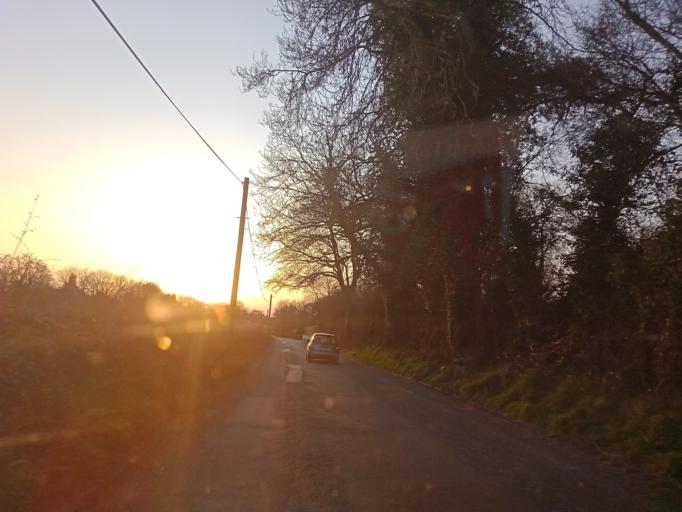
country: IE
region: Leinster
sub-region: Laois
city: Abbeyleix
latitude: 52.8632
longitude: -7.2858
